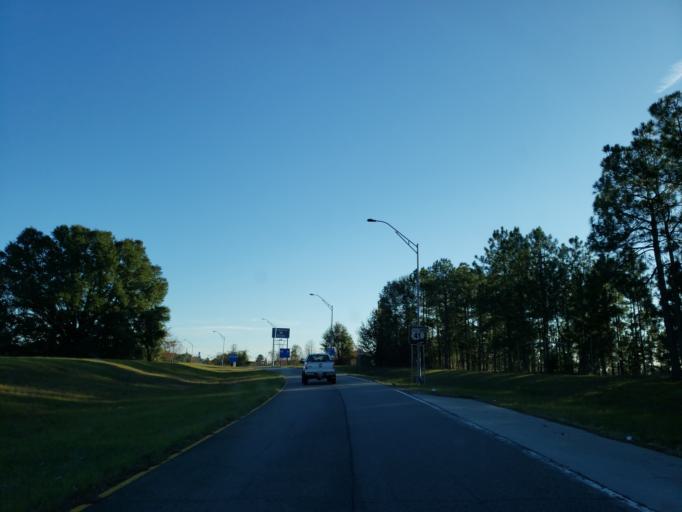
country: US
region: Georgia
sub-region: Dooly County
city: Unadilla
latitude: 32.2487
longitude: -83.7453
